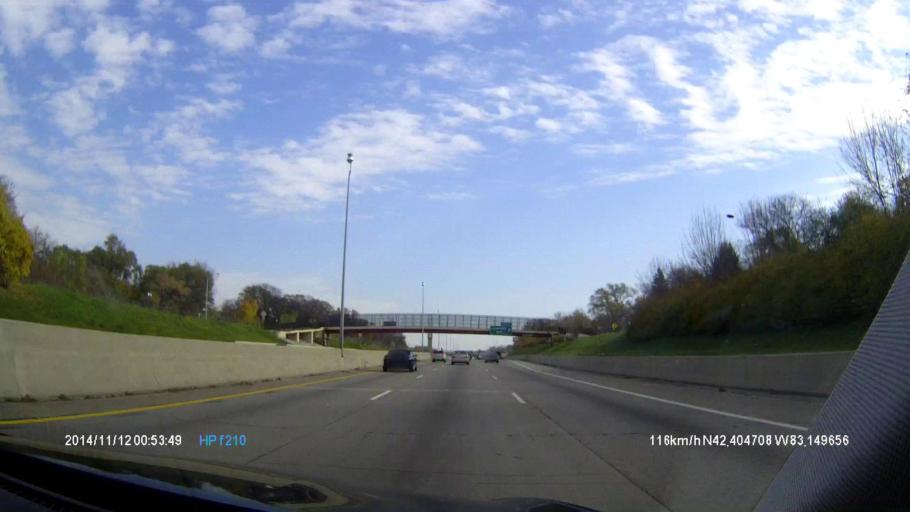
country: US
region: Michigan
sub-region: Wayne County
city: Highland Park
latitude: 42.4047
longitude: -83.1493
